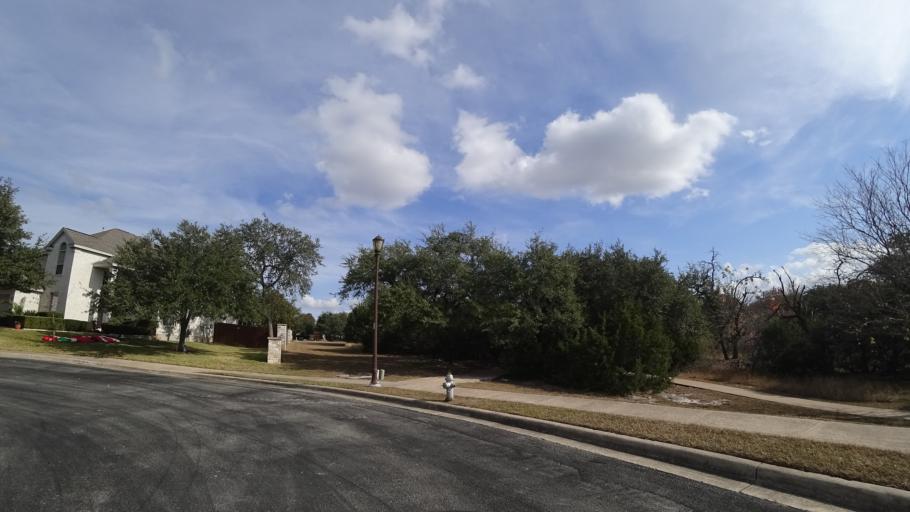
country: US
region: Texas
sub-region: Williamson County
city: Brushy Creek
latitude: 30.5135
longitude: -97.7501
